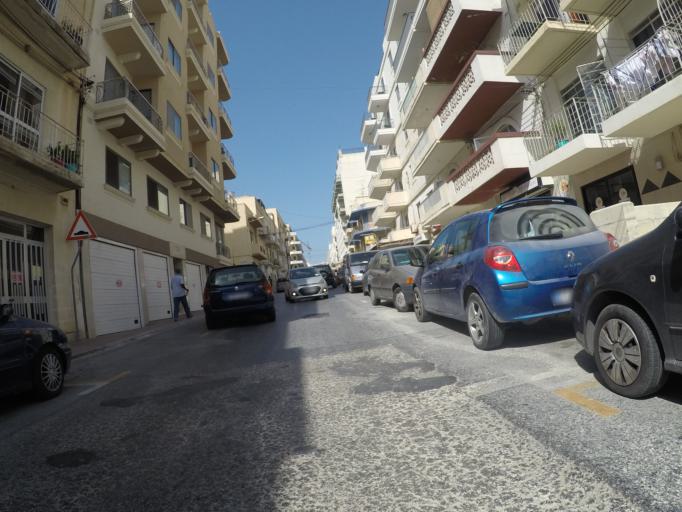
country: MT
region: Saint Paul's Bay
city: San Pawl il-Bahar
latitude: 35.9467
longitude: 14.4090
